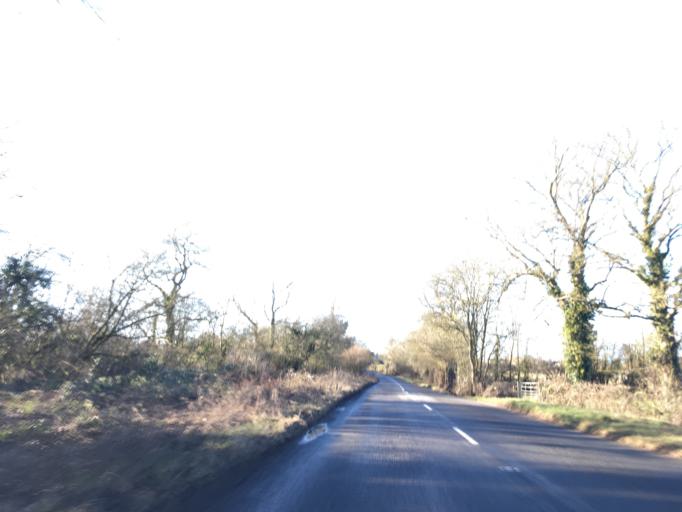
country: GB
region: England
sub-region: Wiltshire
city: Hankerton
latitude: 51.6007
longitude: -2.0422
